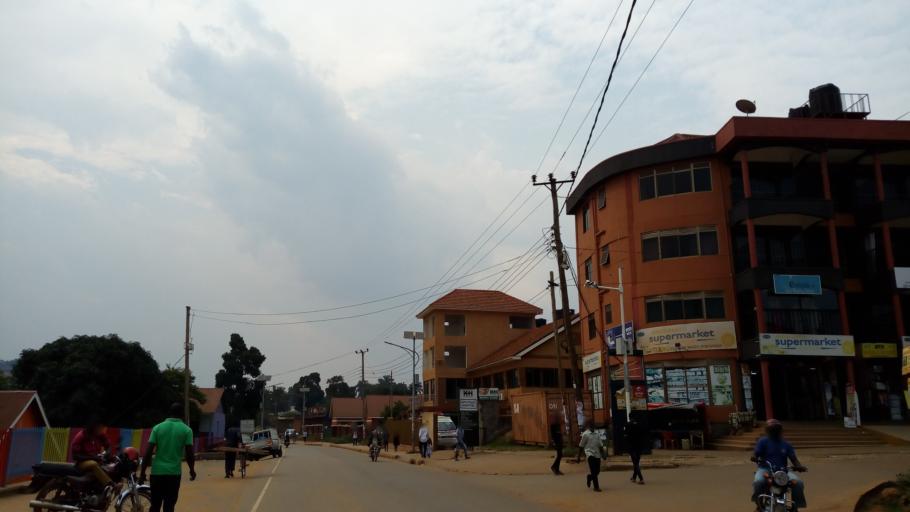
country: UG
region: Central Region
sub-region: Wakiso District
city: Kireka
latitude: 0.3152
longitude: 32.6361
